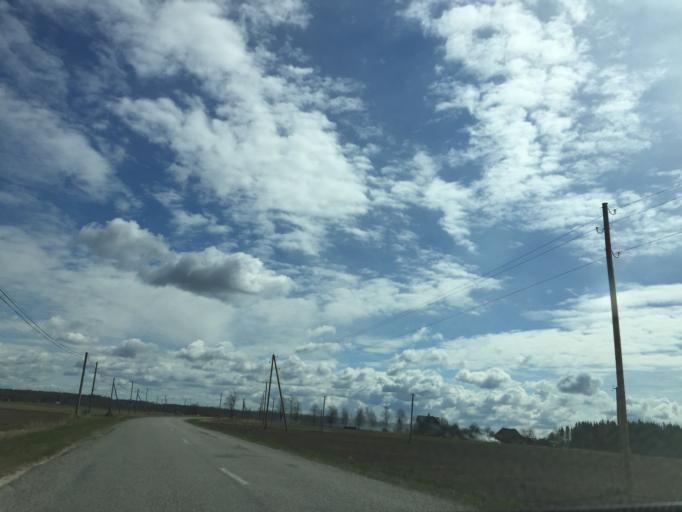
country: LV
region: Salacgrivas
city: Salacgriva
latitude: 57.7459
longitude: 24.3871
